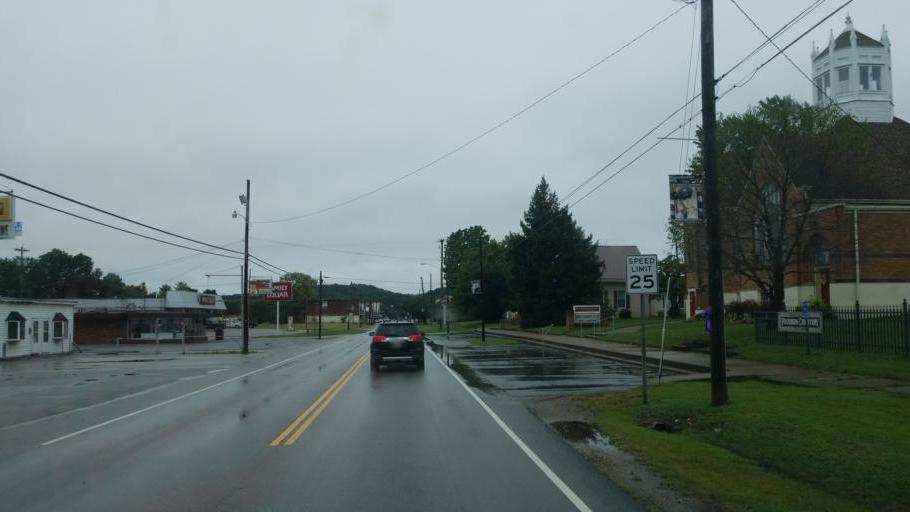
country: US
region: Ohio
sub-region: Adams County
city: Manchester
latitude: 38.6882
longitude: -83.6040
